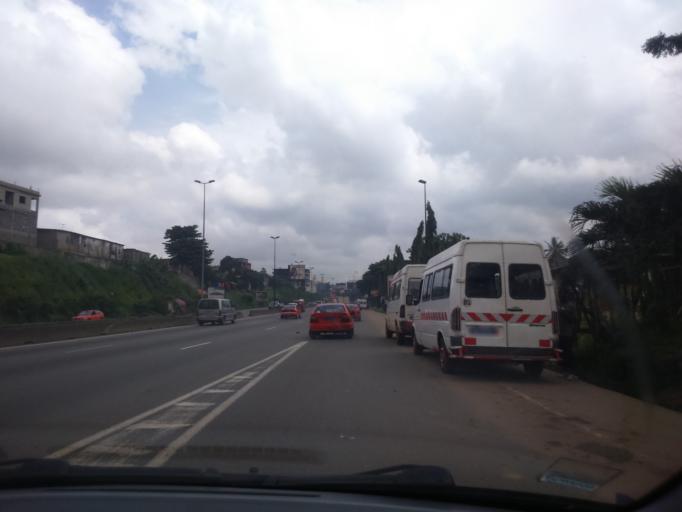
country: CI
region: Lagunes
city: Abidjan
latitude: 5.3610
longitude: -4.0188
